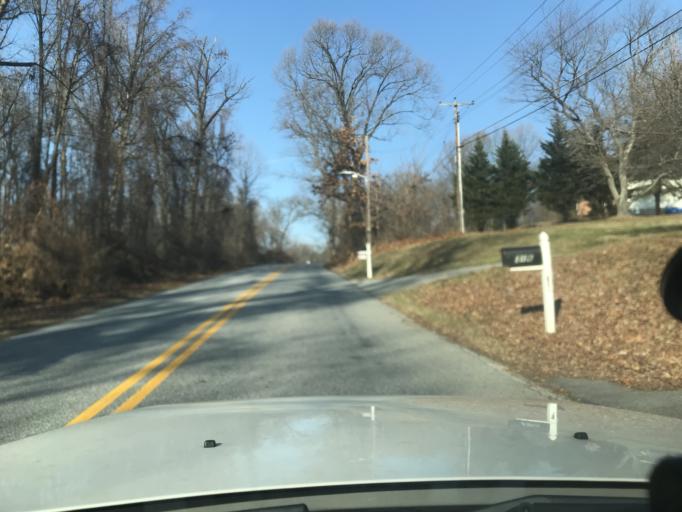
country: US
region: Maryland
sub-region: Baltimore County
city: Owings Mills
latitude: 39.4246
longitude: -76.8034
